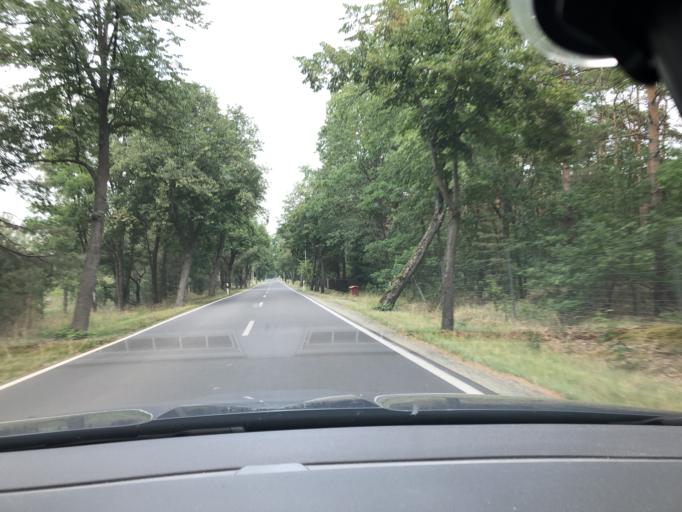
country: DE
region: Brandenburg
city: Kasel-Golzig
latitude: 51.9919
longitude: 13.7793
